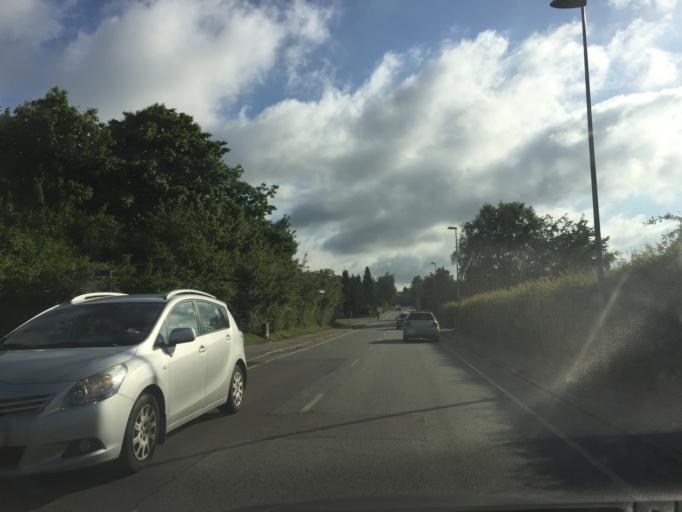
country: DK
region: Zealand
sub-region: Slagelse Kommune
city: Slagelse
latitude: 55.4023
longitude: 11.3782
